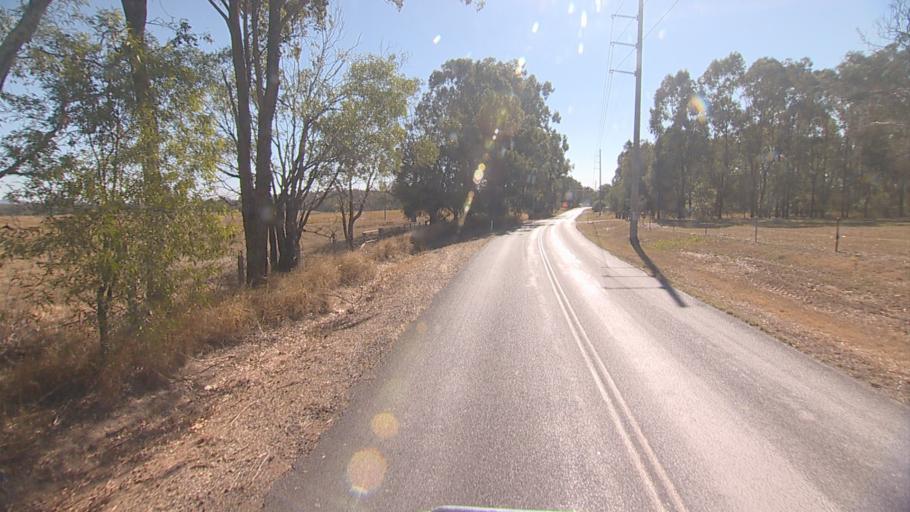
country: AU
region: Queensland
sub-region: Logan
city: Cedar Vale
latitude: -27.8649
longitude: 153.0177
